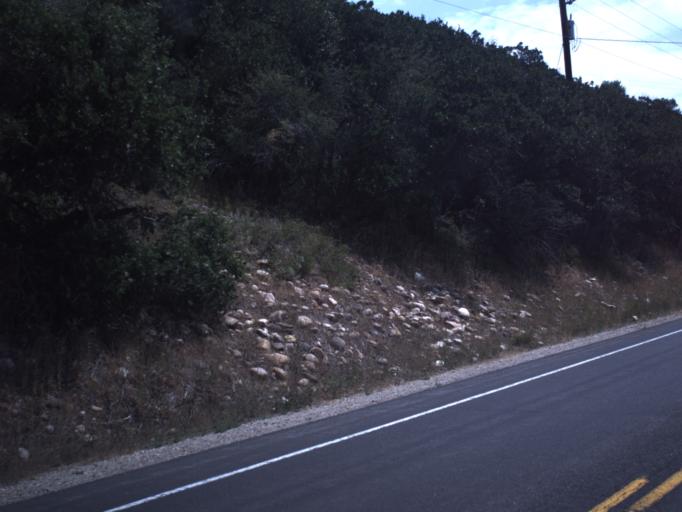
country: US
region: Utah
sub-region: Summit County
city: Francis
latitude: 40.5803
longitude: -111.2242
